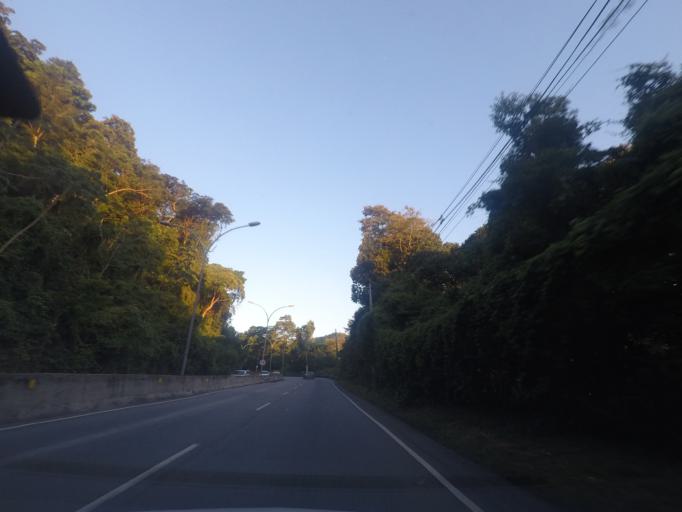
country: BR
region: Rio de Janeiro
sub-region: Rio De Janeiro
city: Rio de Janeiro
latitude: -22.9231
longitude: -43.3095
